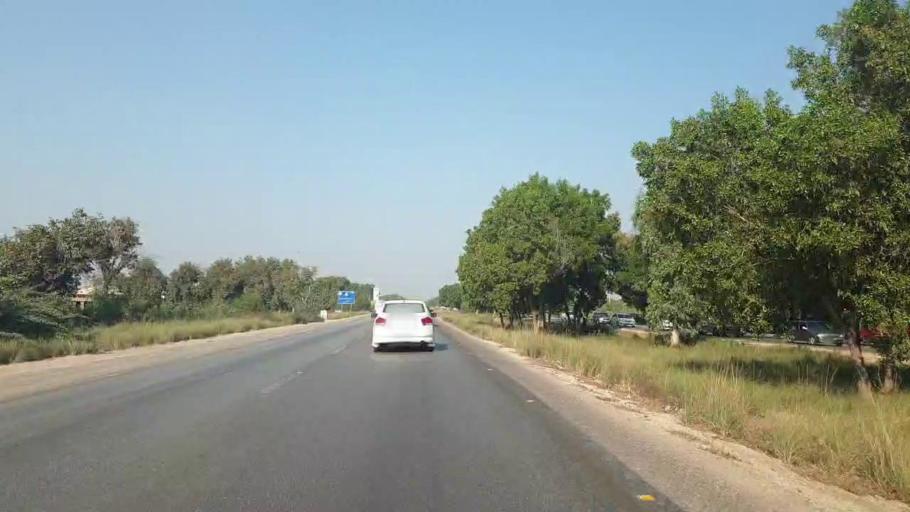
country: PK
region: Sindh
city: Matiari
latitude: 25.5189
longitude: 68.4307
